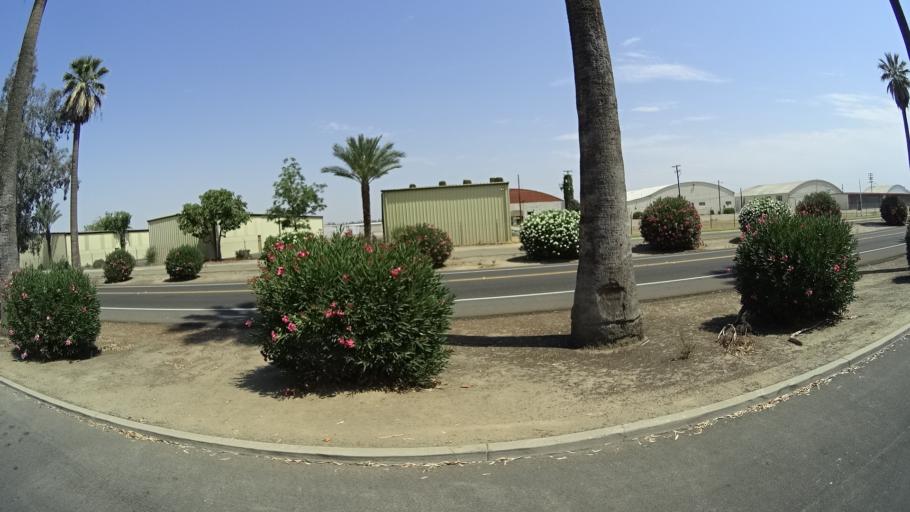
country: US
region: California
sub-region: Fresno County
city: West Park
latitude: 36.7285
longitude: -119.8210
